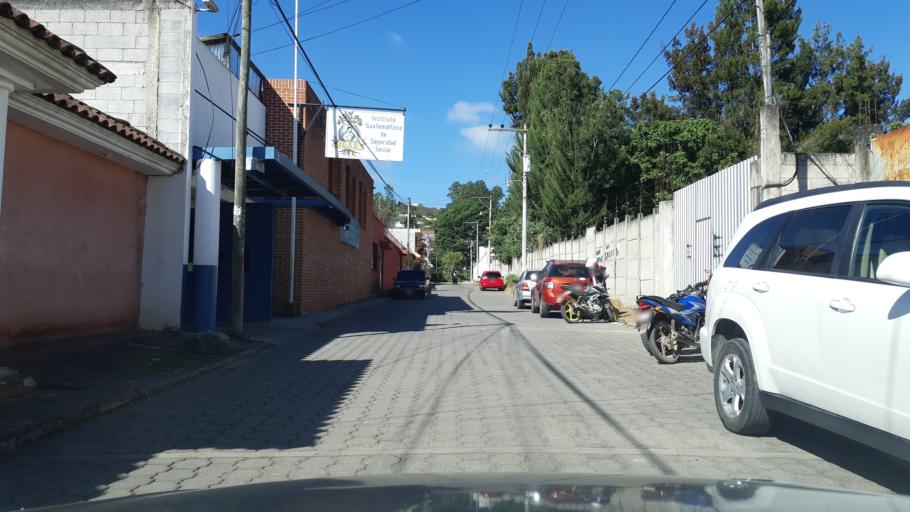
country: GT
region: Chimaltenango
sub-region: Municipio de Chimaltenango
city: Chimaltenango
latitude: 14.6527
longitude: -90.8169
